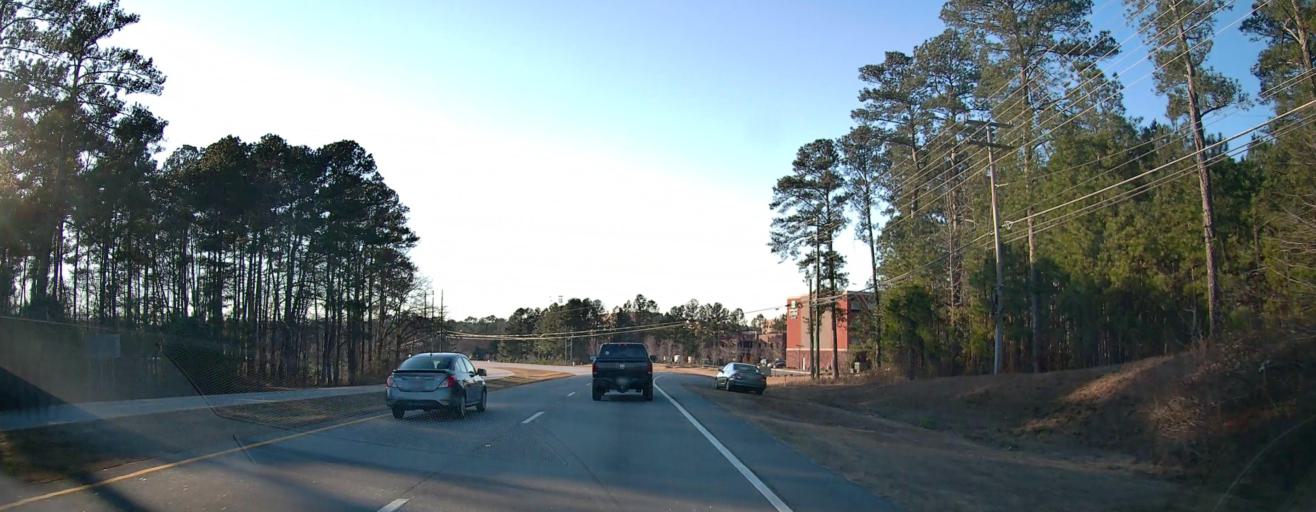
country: US
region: Georgia
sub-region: Fayette County
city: Fayetteville
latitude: 33.4503
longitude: -84.5039
